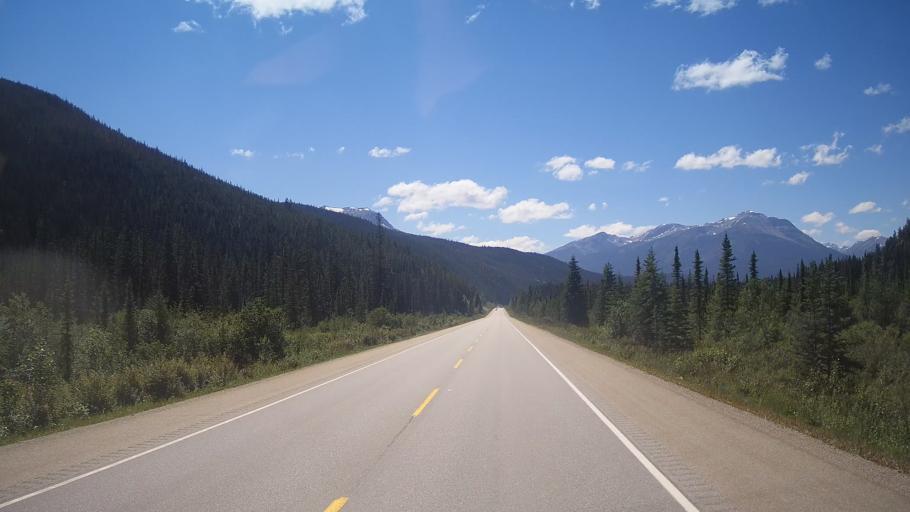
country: CA
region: Alberta
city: Jasper Park Lodge
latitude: 52.8822
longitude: -118.4883
